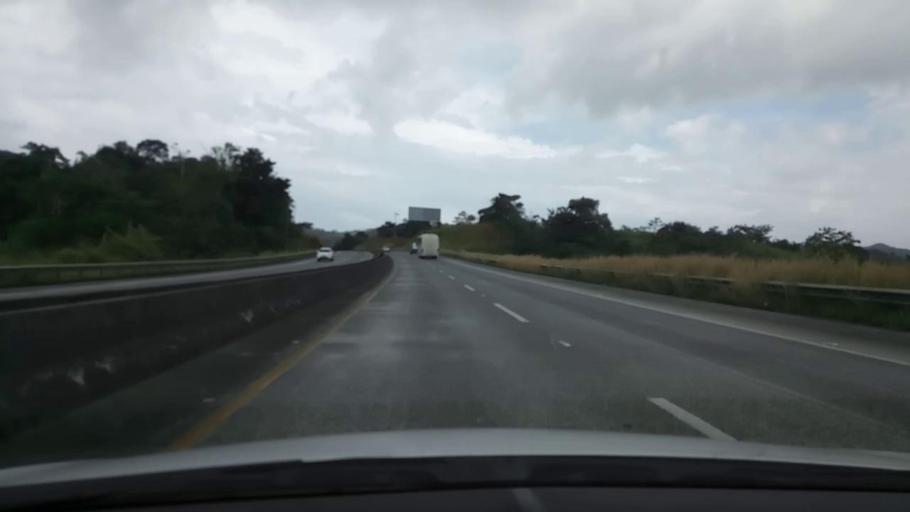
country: PA
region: Colon
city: Gatun
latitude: 9.2804
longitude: -79.7602
